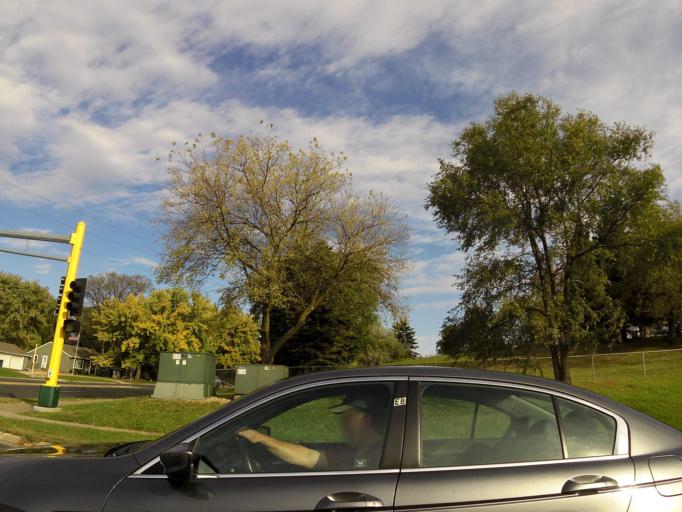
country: US
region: Minnesota
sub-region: Dakota County
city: Eagan
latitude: 44.8045
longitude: -93.1964
